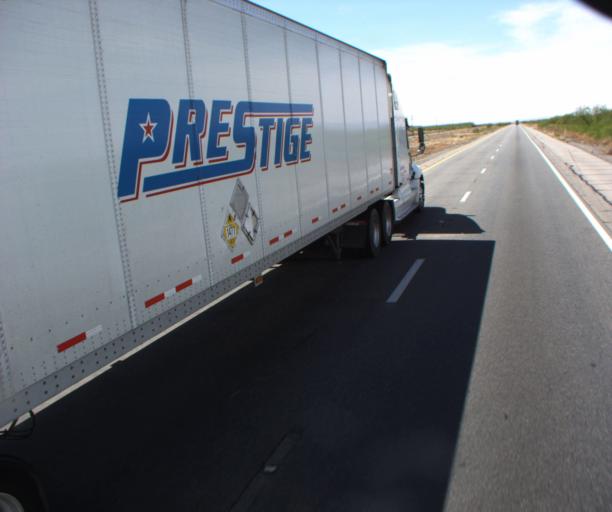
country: US
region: Arizona
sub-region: Cochise County
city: Willcox
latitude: 32.2912
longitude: -109.3263
